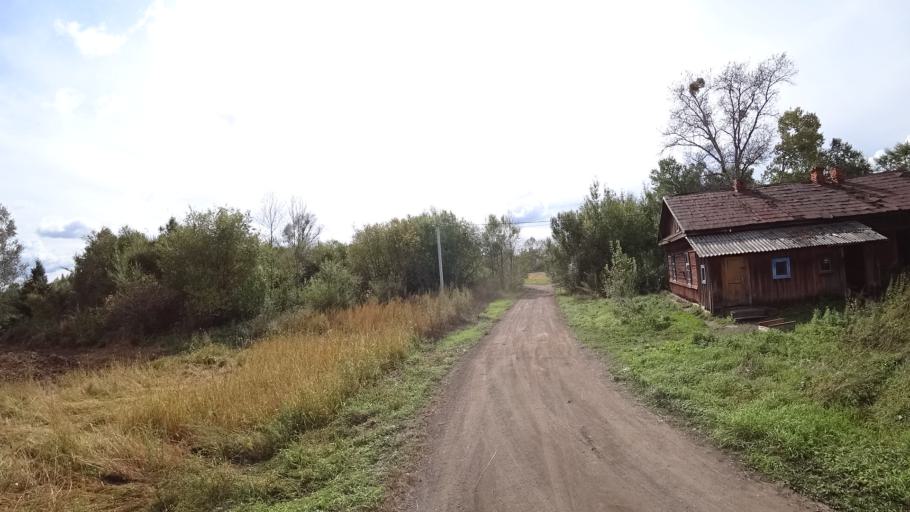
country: RU
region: Amur
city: Arkhara
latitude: 49.3514
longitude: 130.1599
